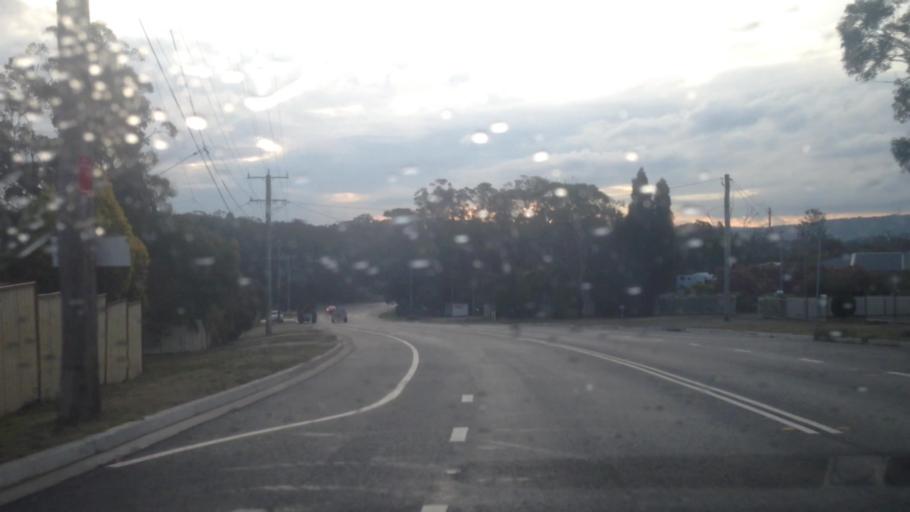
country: AU
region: New South Wales
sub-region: Wyong Shire
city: Charmhaven
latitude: -33.1843
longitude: 151.4902
